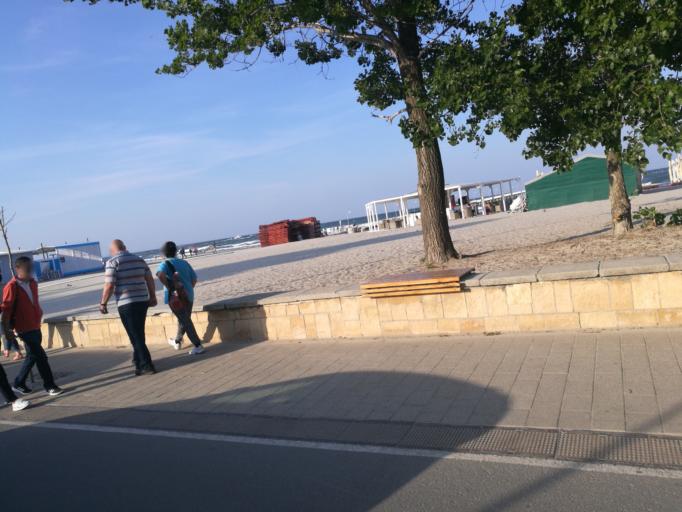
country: RO
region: Constanta
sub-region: Municipiul Constanta
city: Palazu Mare
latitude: 44.2298
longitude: 28.6282
